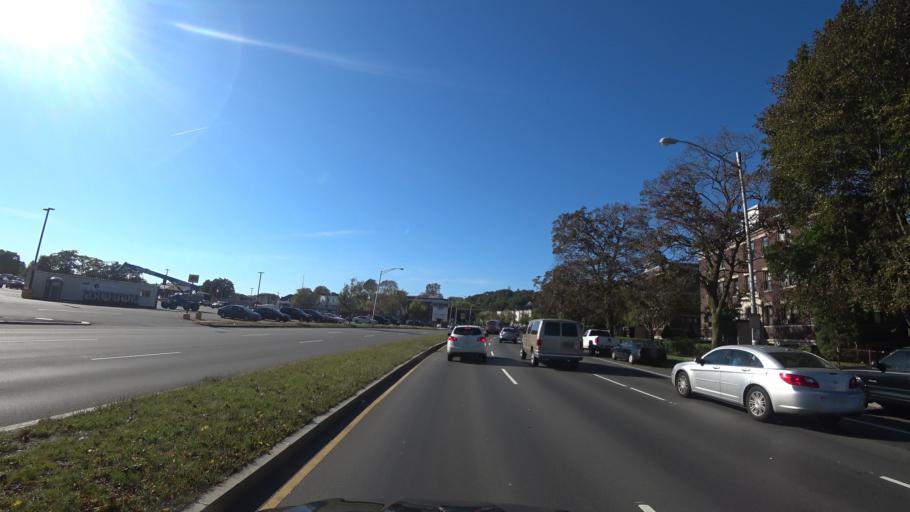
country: US
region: Massachusetts
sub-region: Middlesex County
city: Medford
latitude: 42.4234
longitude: -71.0882
